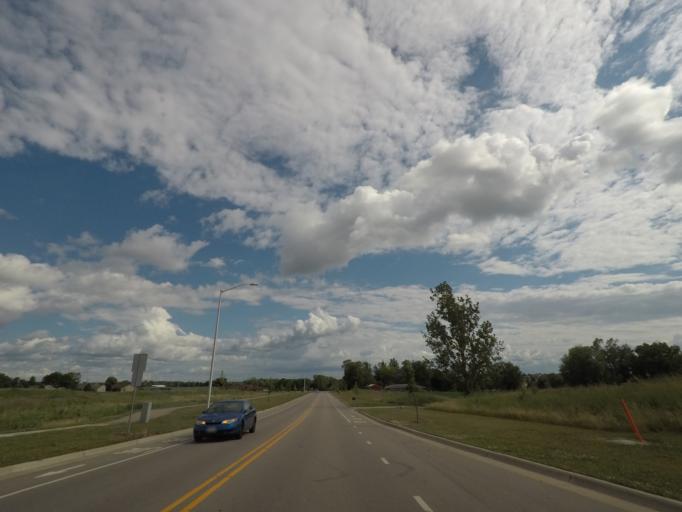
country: US
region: Wisconsin
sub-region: Rock County
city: Janesville
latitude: 42.6819
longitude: -89.0714
